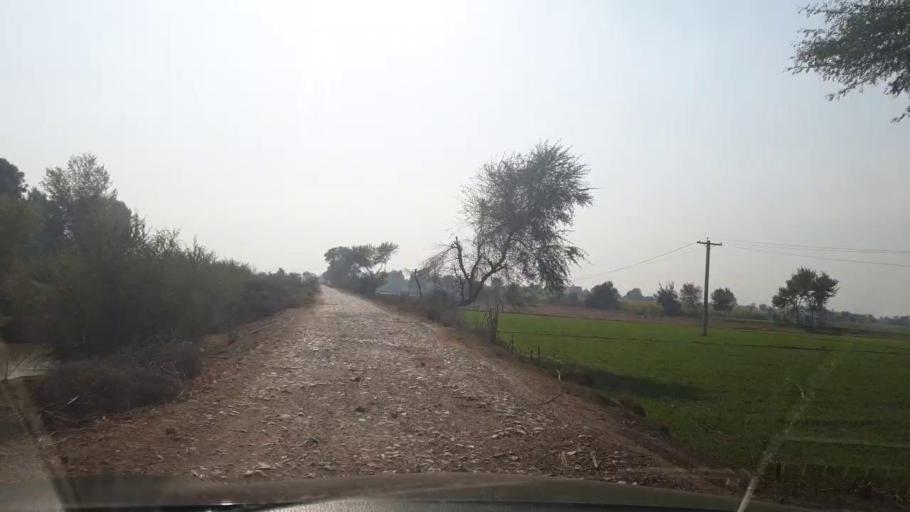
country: PK
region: Sindh
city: Khairpur
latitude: 28.1195
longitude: 69.6417
